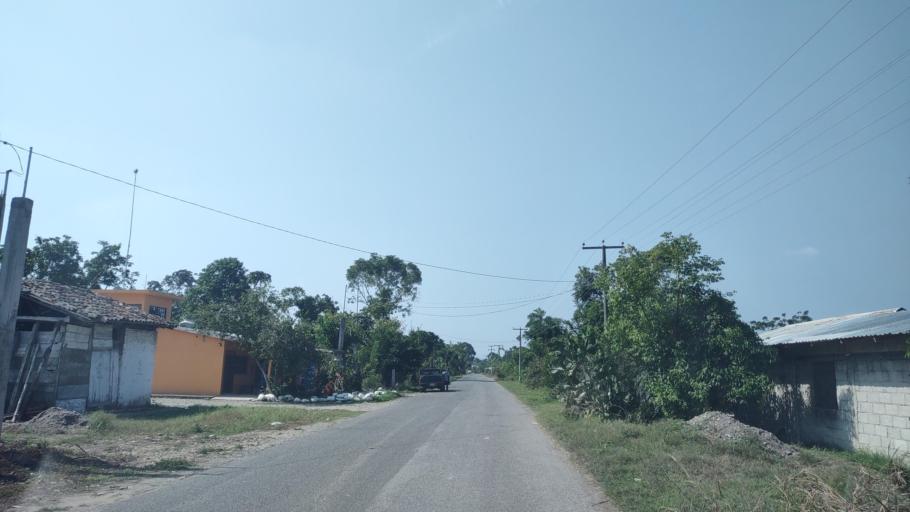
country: MX
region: Puebla
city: Espinal
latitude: 20.2571
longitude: -97.3233
